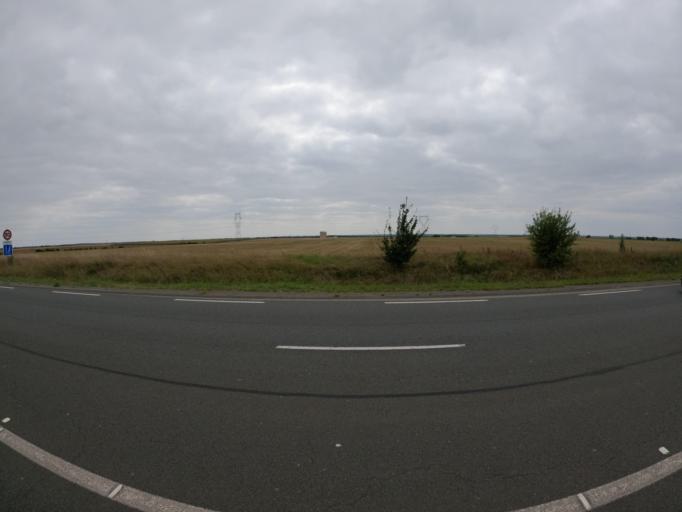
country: FR
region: Poitou-Charentes
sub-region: Departement des Deux-Sevres
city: Mougon
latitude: 46.3007
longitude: -0.3211
